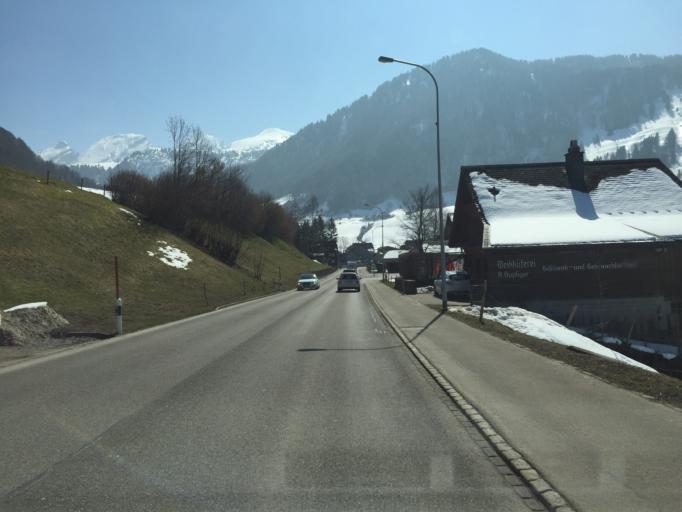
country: CH
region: Saint Gallen
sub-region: Wahlkreis Toggenburg
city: Krummenau
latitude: 47.2014
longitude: 9.2263
